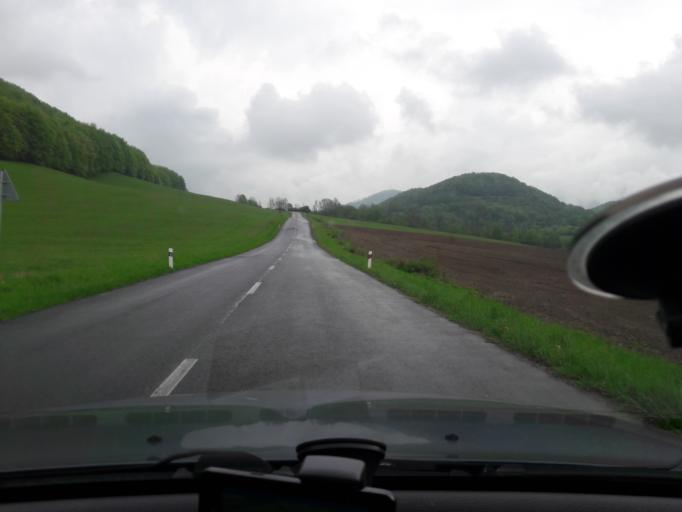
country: SK
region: Banskobystricky
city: Tisovec
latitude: 48.7299
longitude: 20.0280
